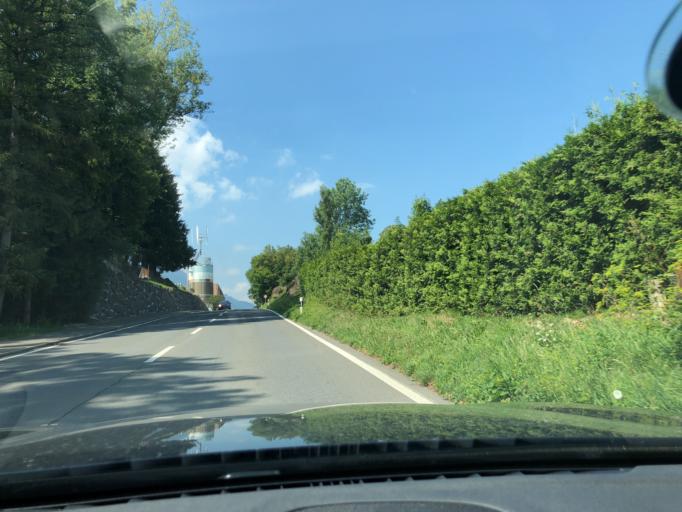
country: CH
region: Schwyz
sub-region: Bezirk Schwyz
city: Goldau
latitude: 47.0401
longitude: 8.5591
